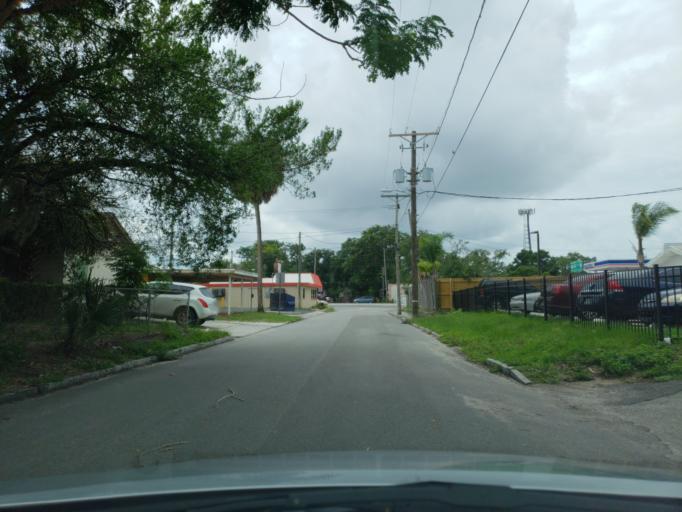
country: US
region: Florida
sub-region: Hillsborough County
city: Tampa
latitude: 27.9970
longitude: -82.4502
